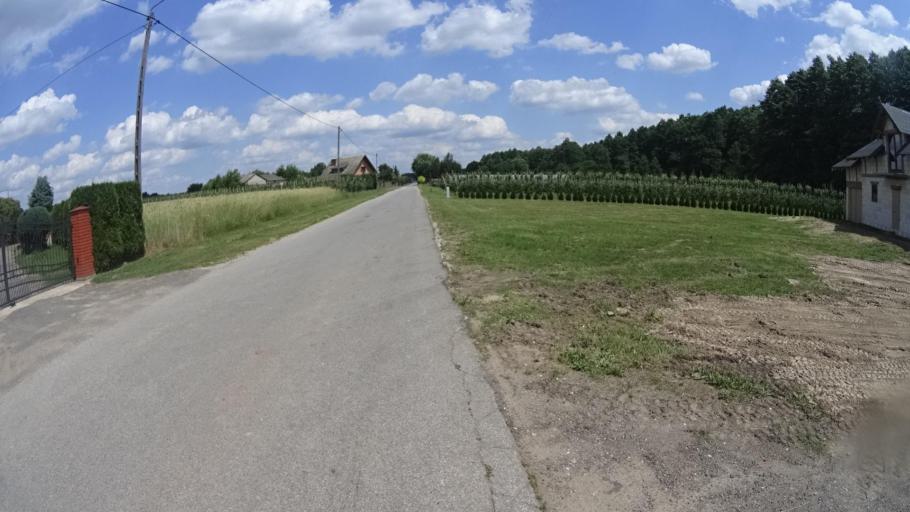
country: PL
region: Masovian Voivodeship
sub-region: Powiat grojecki
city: Goszczyn
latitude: 51.6919
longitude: 20.8632
